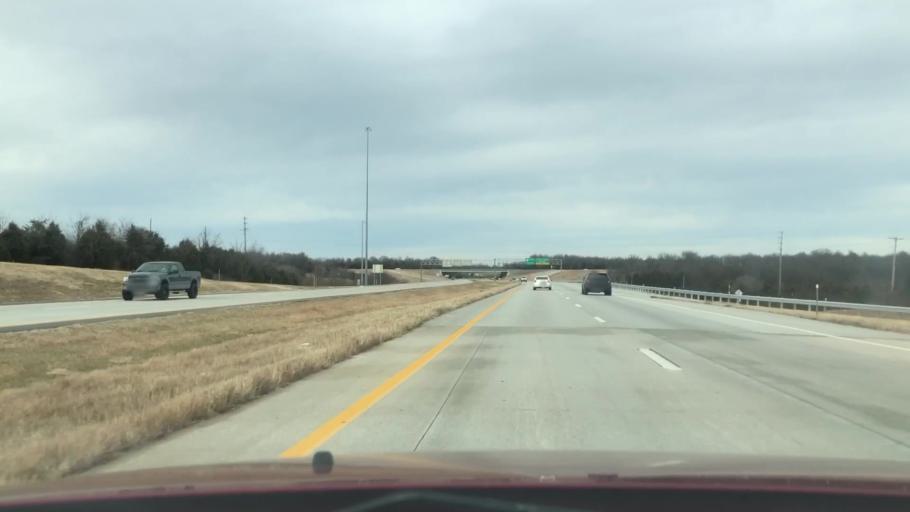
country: US
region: Missouri
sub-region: Greene County
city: Springfield
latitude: 37.2528
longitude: -93.2243
